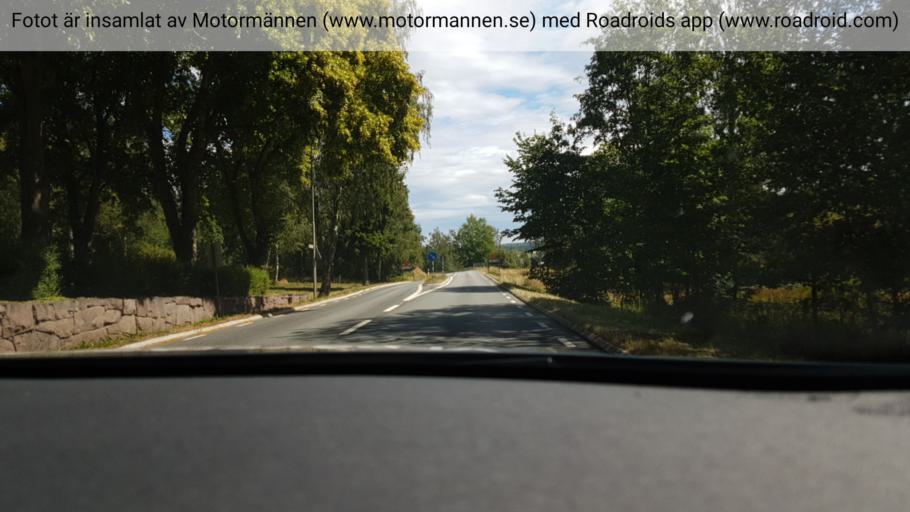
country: SE
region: Joenkoeping
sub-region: Aneby Kommun
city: Aneby
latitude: 57.9751
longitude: 14.8044
